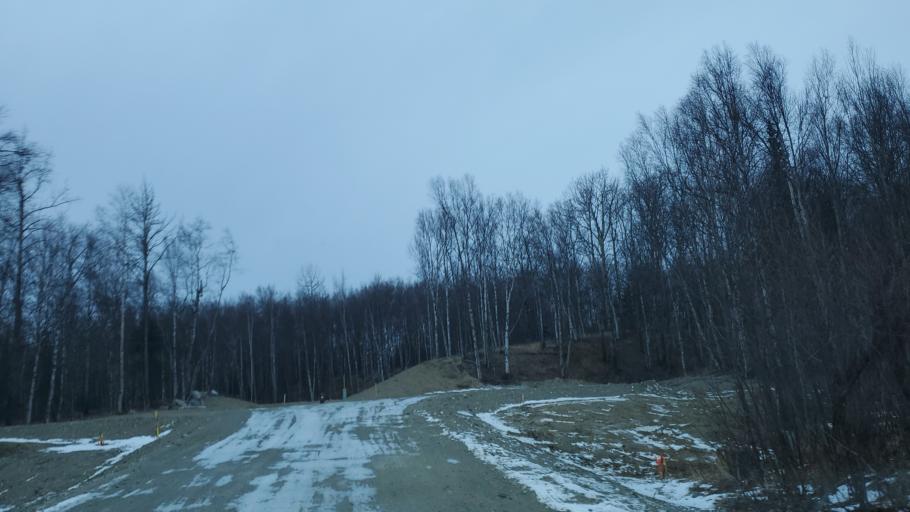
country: US
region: Alaska
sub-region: Matanuska-Susitna Borough
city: Farm Loop
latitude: 61.6565
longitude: -149.2239
